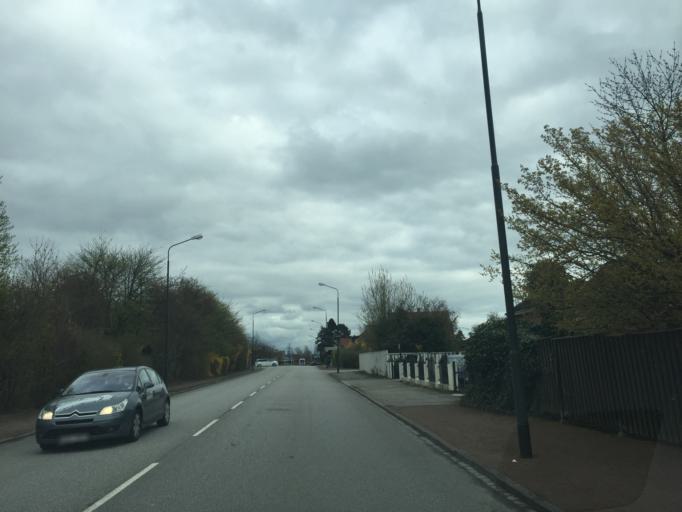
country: SE
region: Skane
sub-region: Malmo
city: Malmoe
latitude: 55.5807
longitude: 12.9724
